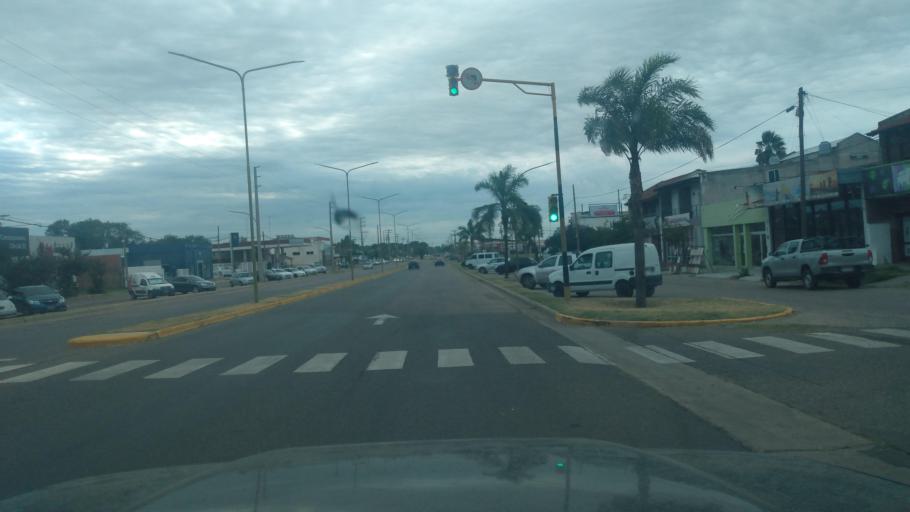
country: AR
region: Buenos Aires
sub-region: Partido de Trenque Lauquen
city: Trenque Lauquen
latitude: -35.9804
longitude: -62.7282
